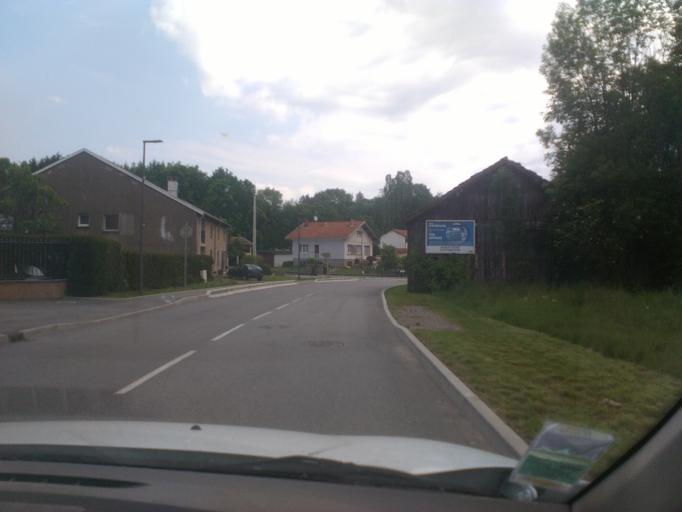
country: FR
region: Lorraine
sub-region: Departement des Vosges
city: Etival-Clairefontaine
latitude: 48.3618
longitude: 6.8485
